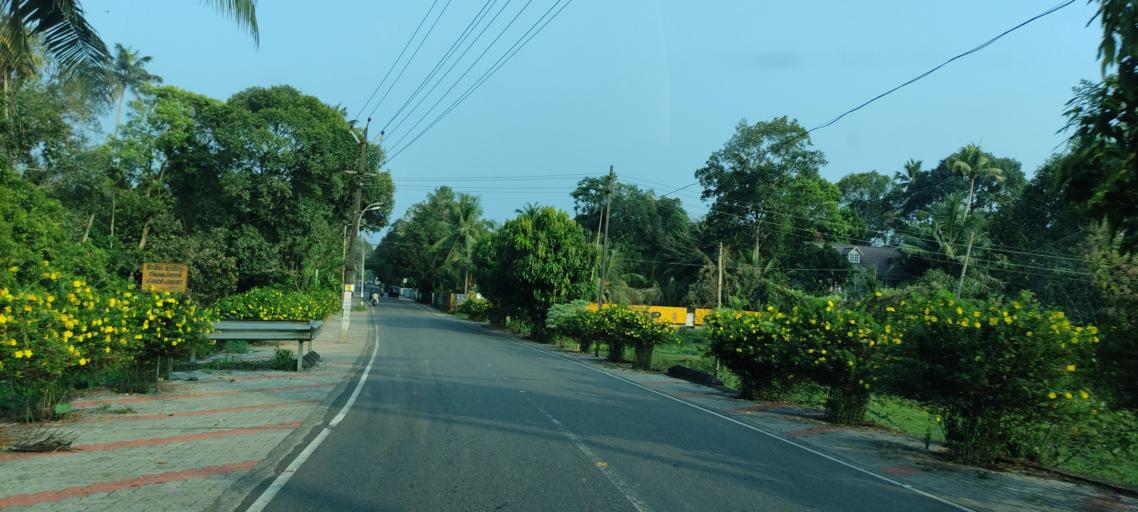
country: IN
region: Kerala
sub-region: Alappuzha
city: Shertallai
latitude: 9.6545
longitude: 76.3402
